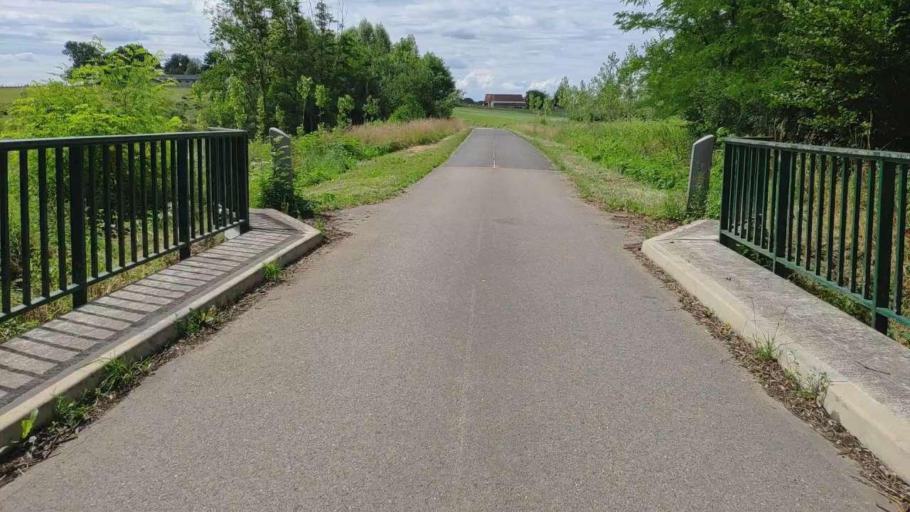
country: FR
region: Franche-Comte
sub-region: Departement du Jura
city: Chaussin
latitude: 46.8724
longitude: 5.4057
